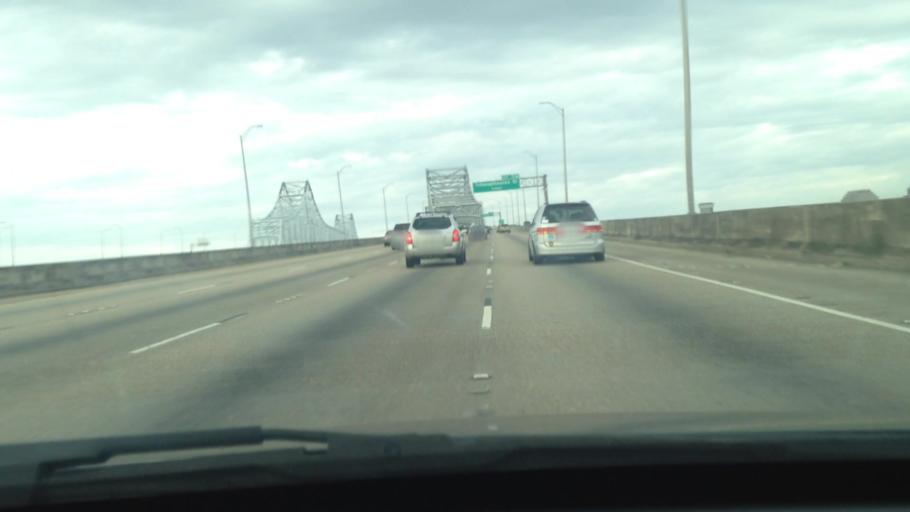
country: US
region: Louisiana
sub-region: Jefferson Parish
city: Gretna
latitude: 29.9388
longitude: -90.0461
